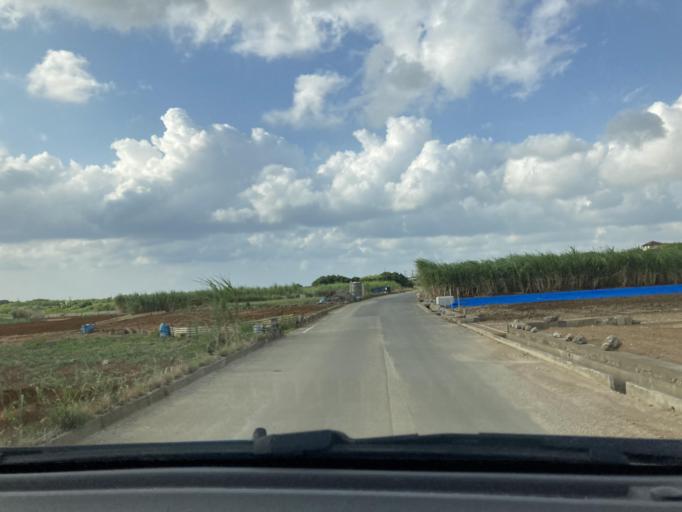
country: JP
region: Okinawa
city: Itoman
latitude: 26.0827
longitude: 127.6634
